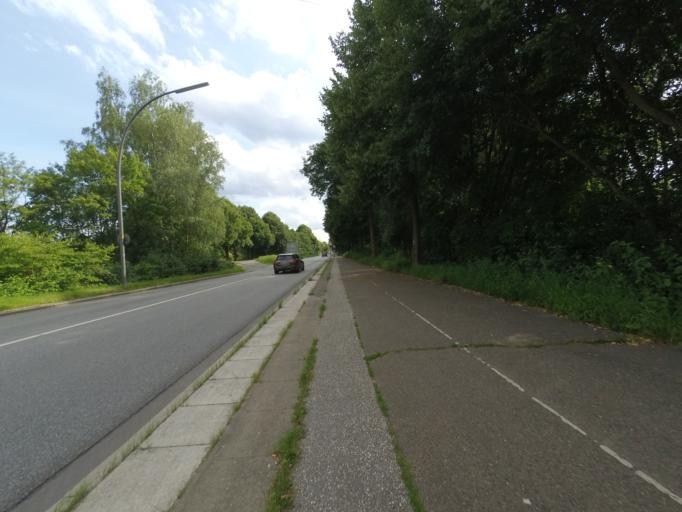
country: DE
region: Hamburg
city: Bergedorf
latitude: 53.4737
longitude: 10.2047
